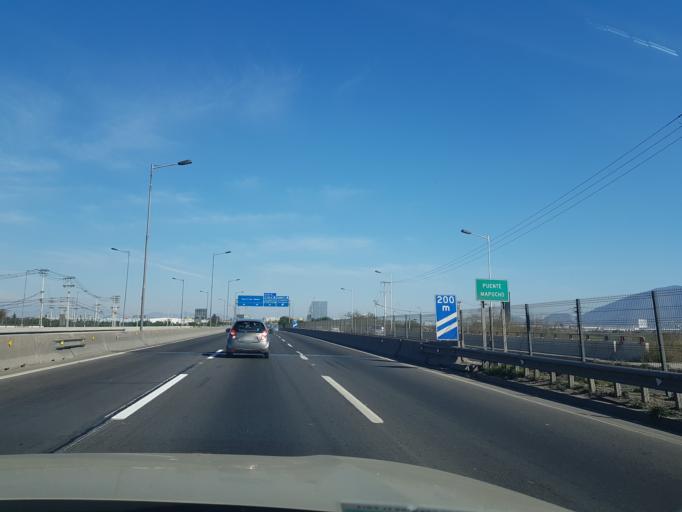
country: CL
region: Santiago Metropolitan
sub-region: Provincia de Santiago
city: Lo Prado
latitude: -33.4132
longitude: -70.7825
